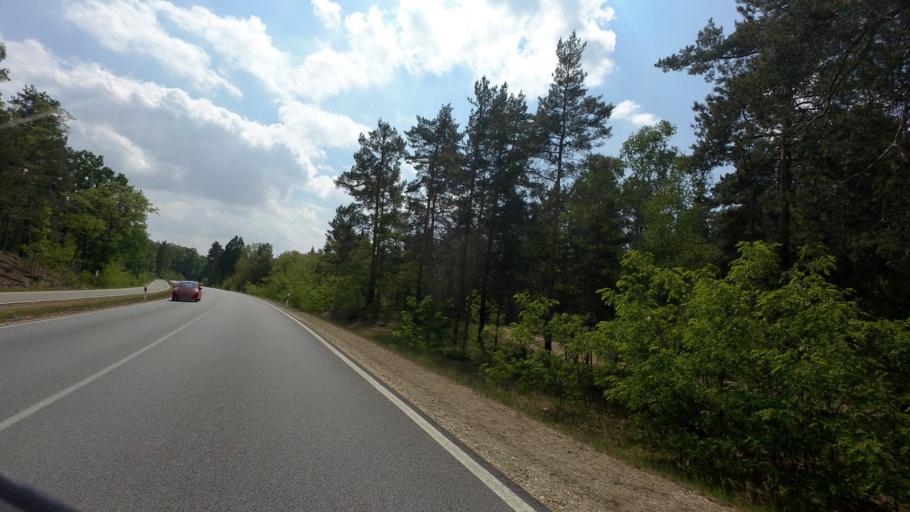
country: DE
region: Saxony
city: Rietschen
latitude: 51.4167
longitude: 14.7883
